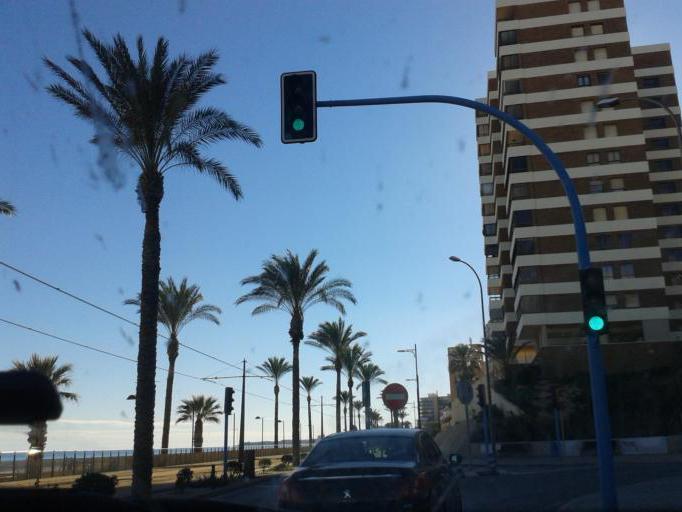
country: ES
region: Valencia
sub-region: Provincia de Alicante
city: el Campello
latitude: 38.4080
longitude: -0.4033
